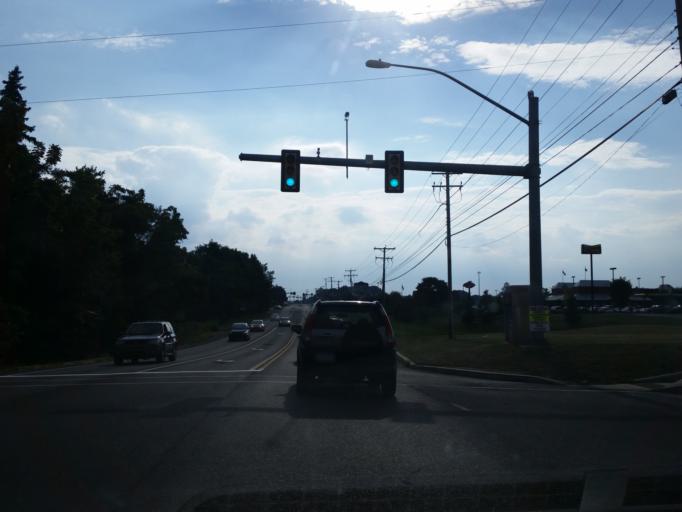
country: US
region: Pennsylvania
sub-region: Lebanon County
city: Palmyra
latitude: 40.3200
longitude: -76.5621
